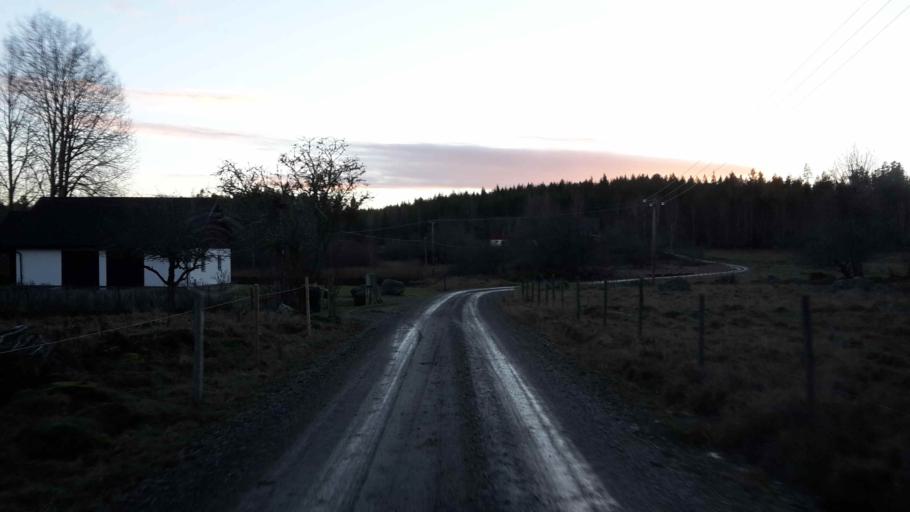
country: SE
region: OEstergoetland
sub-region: Atvidabergs Kommun
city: Atvidaberg
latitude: 58.2702
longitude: 16.0751
